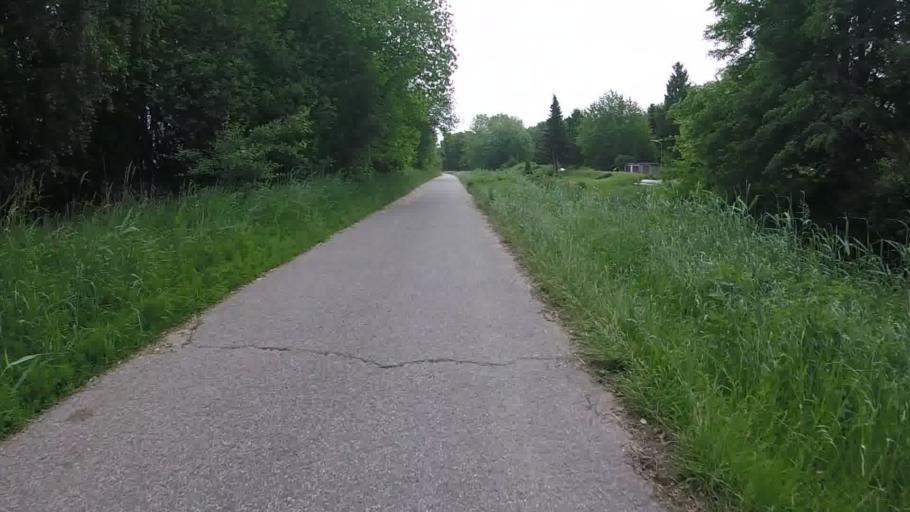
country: DE
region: Schleswig-Holstein
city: Oststeinbek
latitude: 53.4961
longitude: 10.1373
